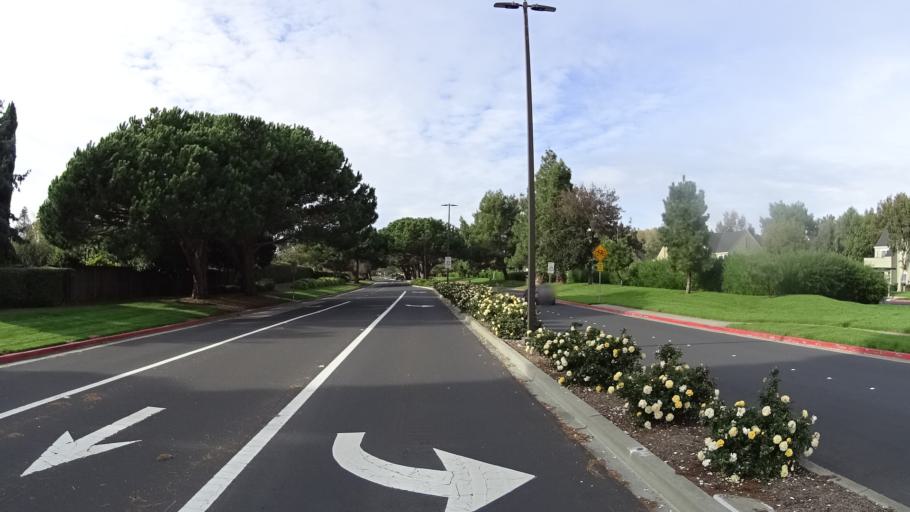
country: US
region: California
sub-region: San Mateo County
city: Redwood Shores
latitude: 37.5335
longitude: -122.2423
